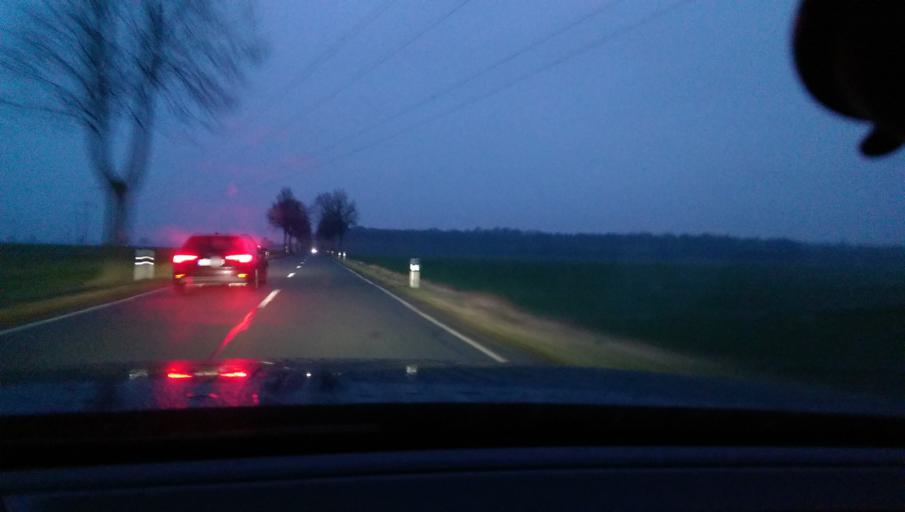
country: DE
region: Lower Saxony
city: Gross Munzel
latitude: 52.3807
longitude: 9.5113
